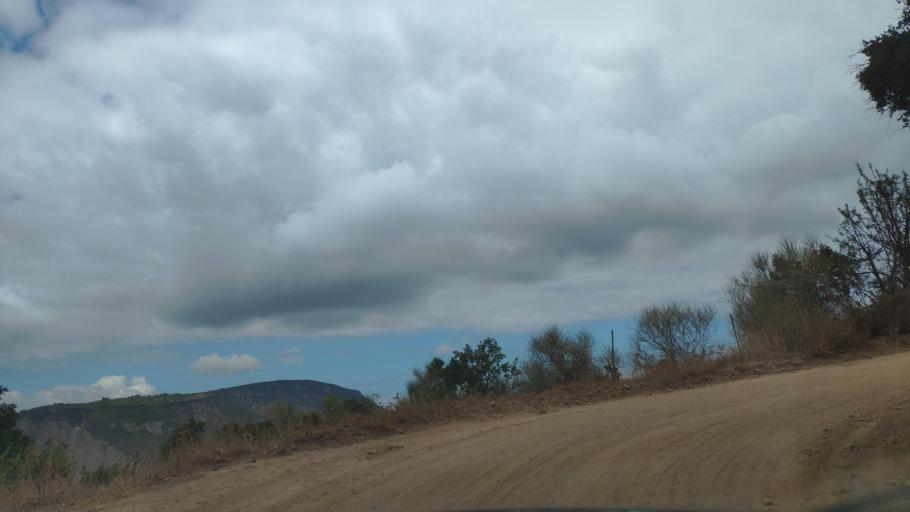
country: GR
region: West Greece
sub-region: Nomos Achaias
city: Temeni
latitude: 38.1627
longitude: 22.1440
